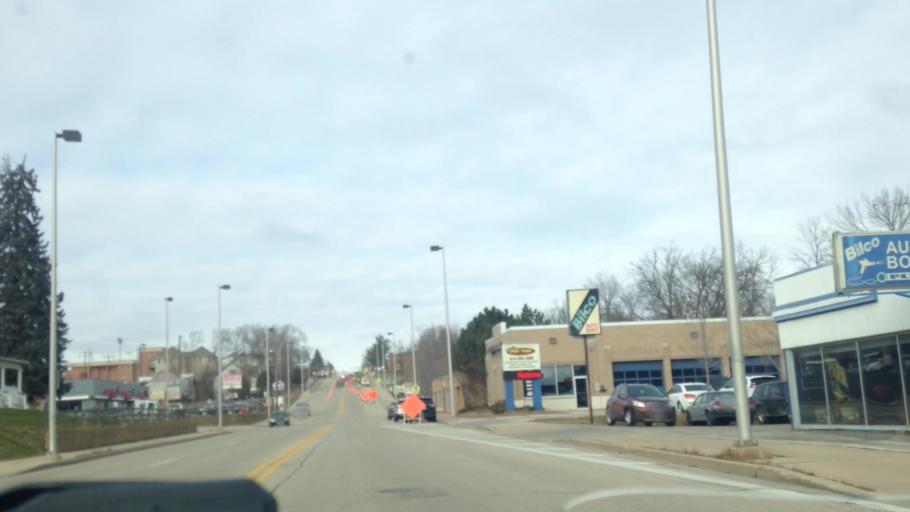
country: US
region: Wisconsin
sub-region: Waukesha County
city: Menomonee Falls
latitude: 43.1748
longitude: -88.1130
